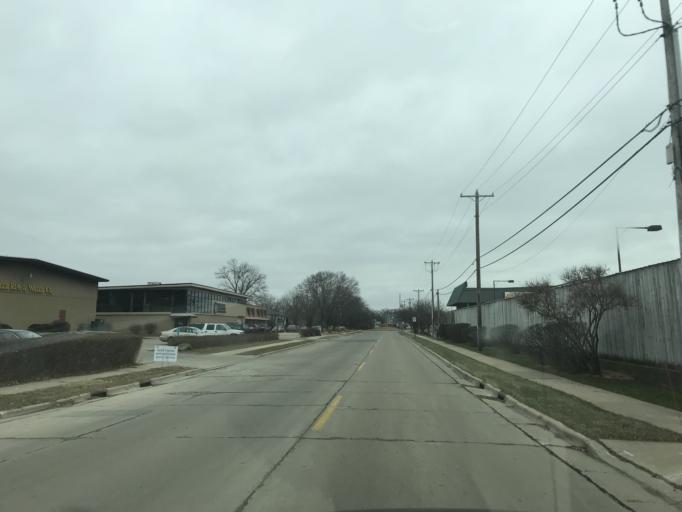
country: US
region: Wisconsin
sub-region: Dane County
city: Monona
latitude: 43.0506
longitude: -89.3126
